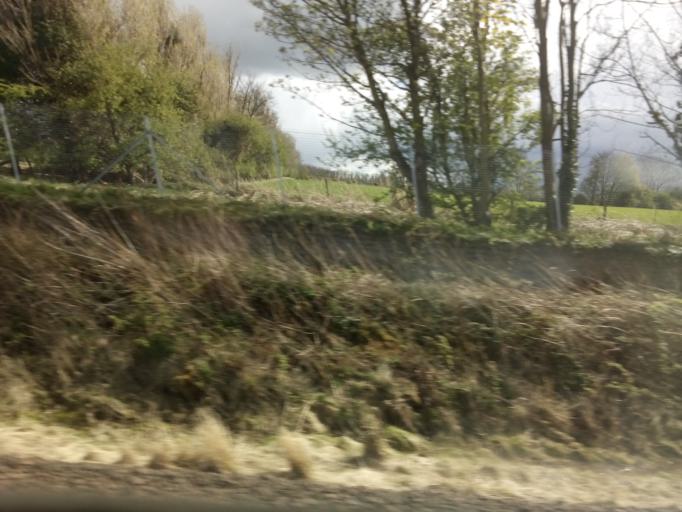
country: GB
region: Scotland
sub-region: East Lothian
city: Longniddry
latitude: 55.9788
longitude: -2.8808
